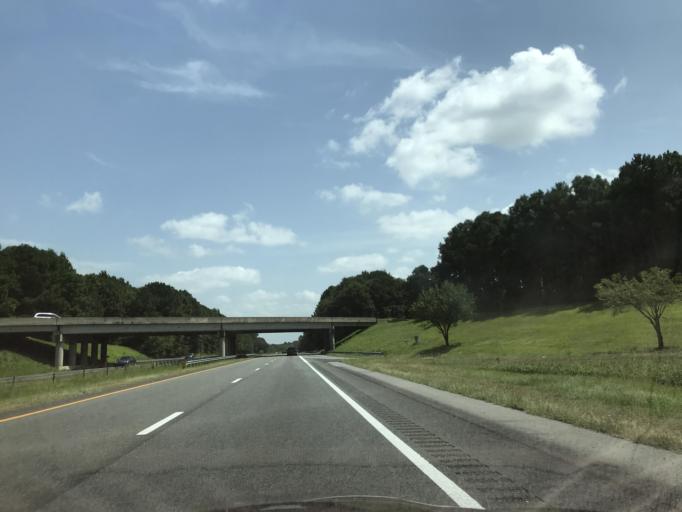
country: US
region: North Carolina
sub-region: Sampson County
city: Plain View
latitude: 35.2264
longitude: -78.3497
